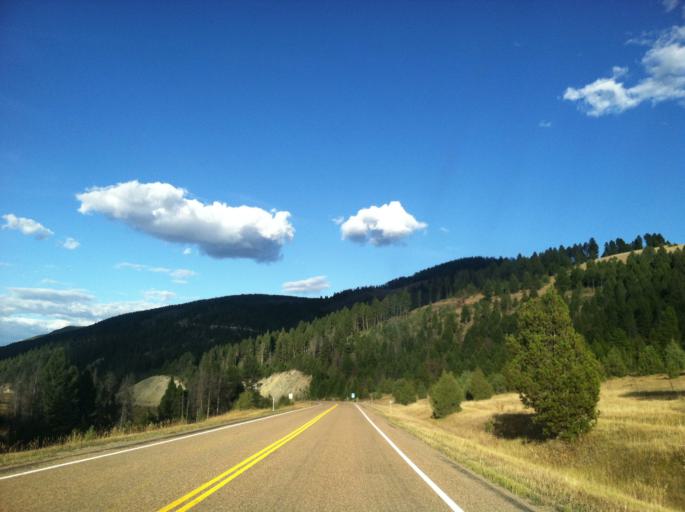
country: US
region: Montana
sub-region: Granite County
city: Philipsburg
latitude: 46.3998
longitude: -113.3017
